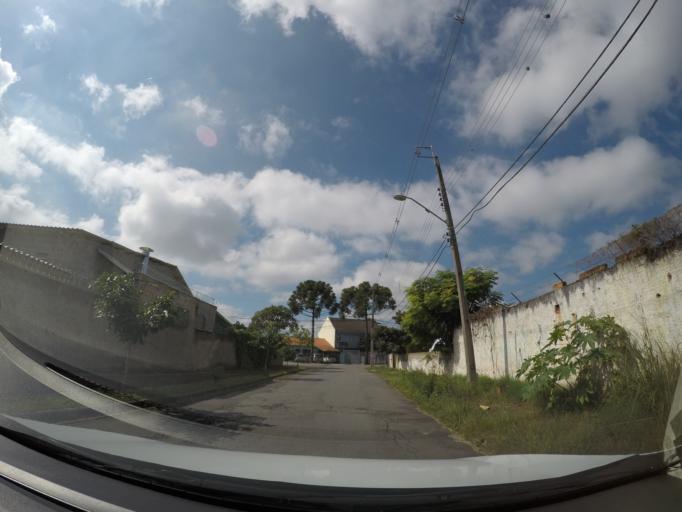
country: BR
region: Parana
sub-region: Sao Jose Dos Pinhais
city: Sao Jose dos Pinhais
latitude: -25.4941
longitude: -49.2232
